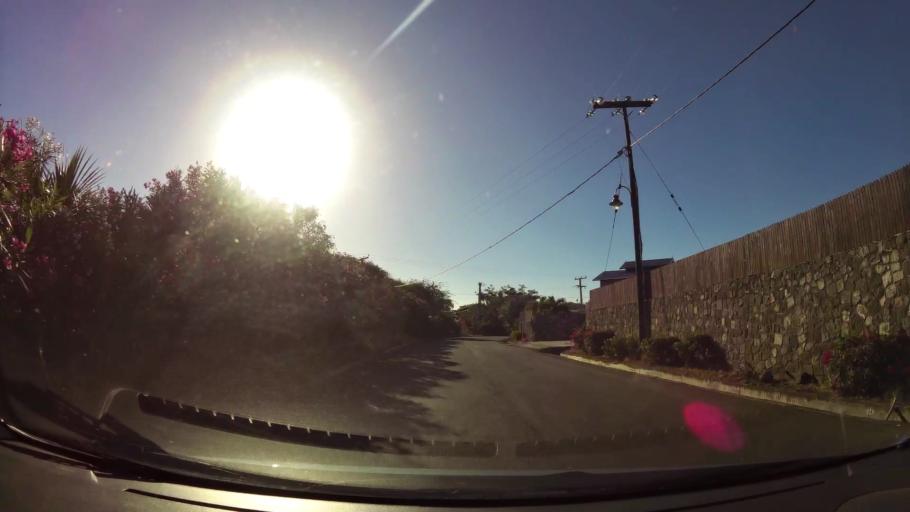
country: MU
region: Black River
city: Tamarin
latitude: -20.3352
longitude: 57.3789
